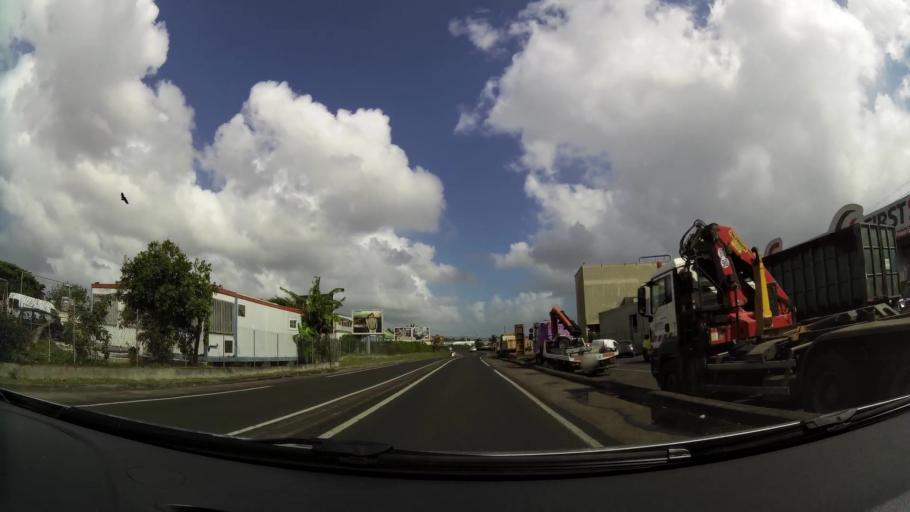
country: MQ
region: Martinique
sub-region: Martinique
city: Fort-de-France
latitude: 14.5962
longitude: -61.0568
